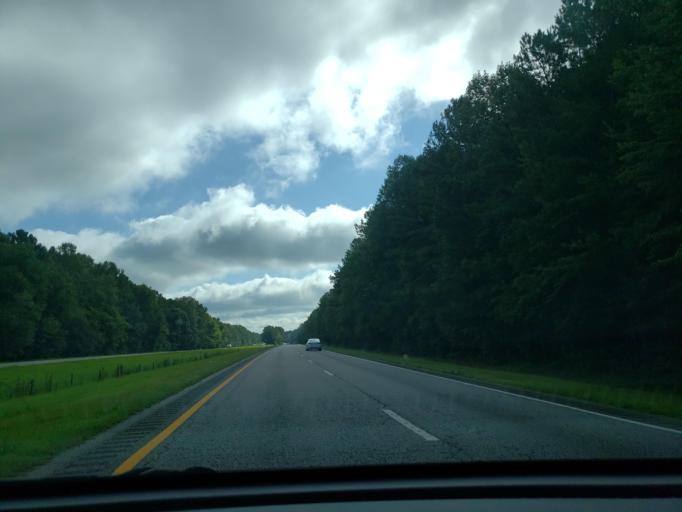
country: US
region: North Carolina
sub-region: Nash County
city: Spring Hope
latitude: 35.9455
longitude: -78.0394
